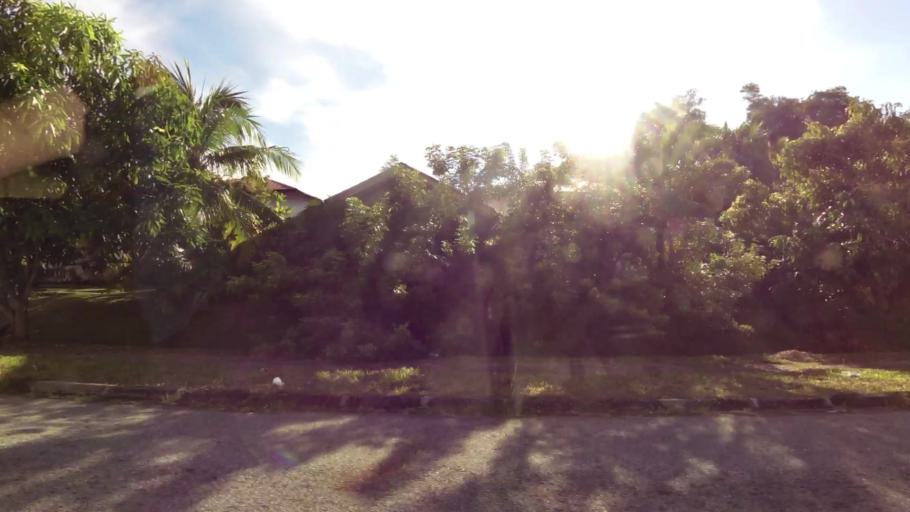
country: BN
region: Brunei and Muara
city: Bandar Seri Begawan
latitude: 4.9823
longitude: 114.9650
